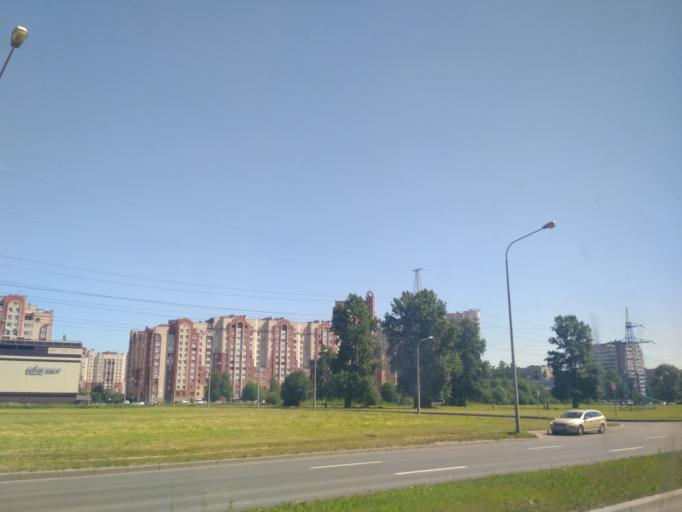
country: RU
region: Leningrad
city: Kalininskiy
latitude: 59.9783
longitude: 30.3872
